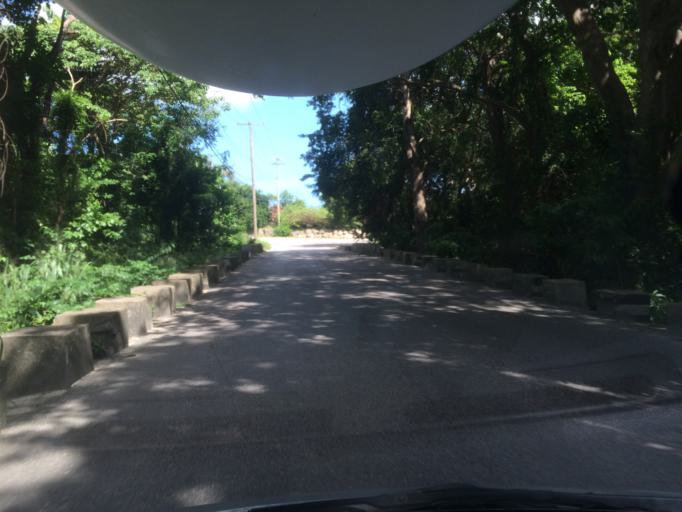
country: BB
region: Saint Lucy
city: Checker Hall
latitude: 13.2960
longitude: -59.6414
